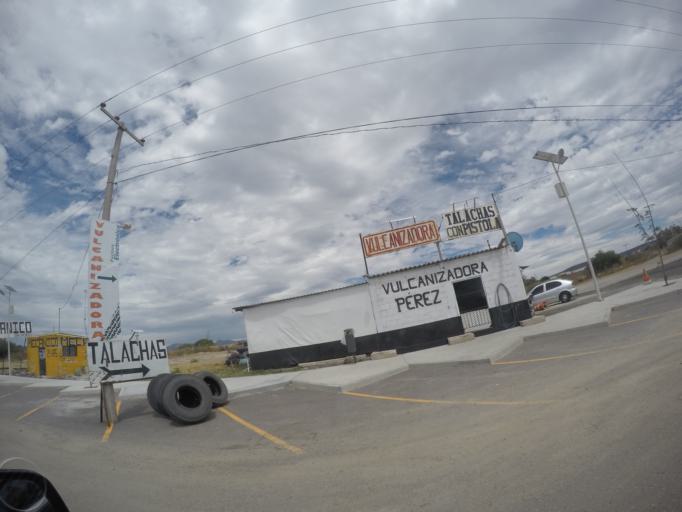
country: MX
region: Queretaro
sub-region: San Juan del Rio
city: Paso de Mata
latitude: 20.3276
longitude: -99.9356
